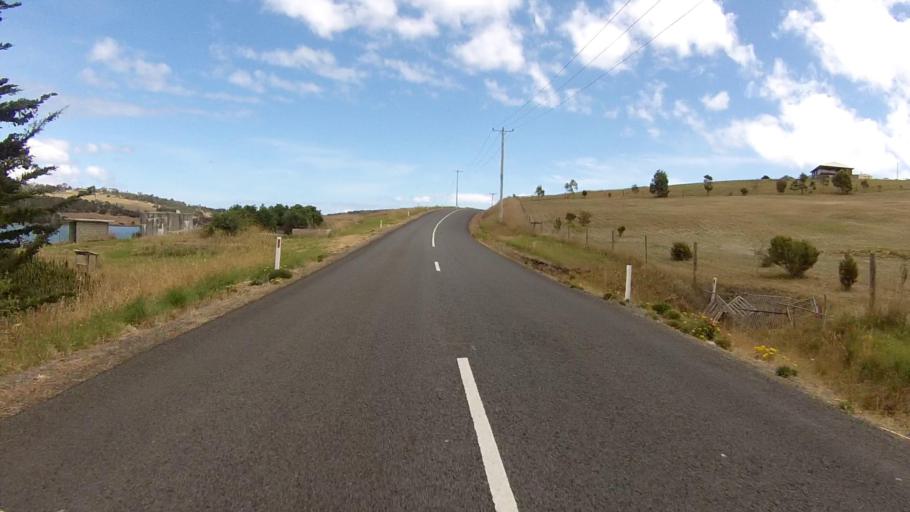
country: AU
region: Tasmania
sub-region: Sorell
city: Sorell
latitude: -42.8680
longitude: 147.6737
